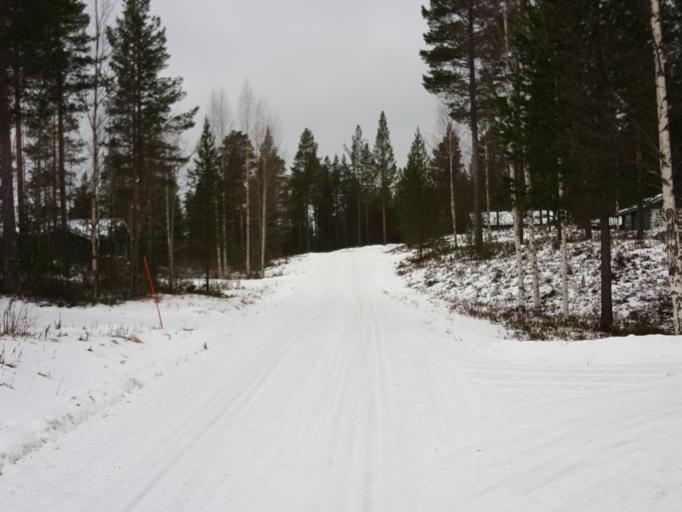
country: SE
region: Jaemtland
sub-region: Harjedalens Kommun
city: Sveg
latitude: 62.4227
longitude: 13.9353
